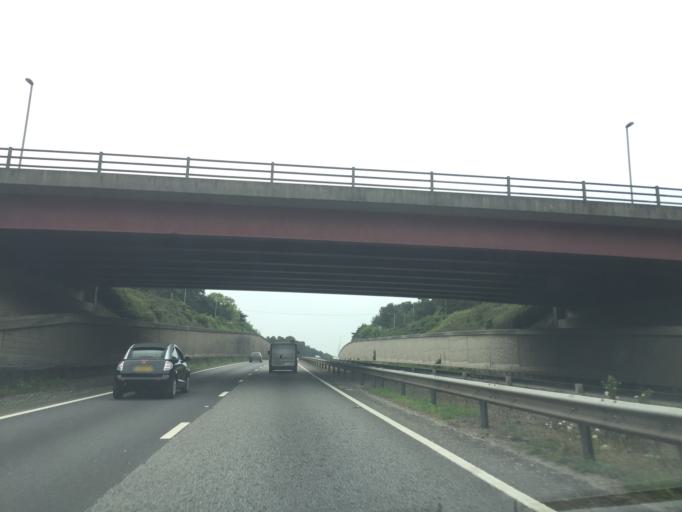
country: GB
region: England
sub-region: Hampshire
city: Ringwood
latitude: 50.8390
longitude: -1.8133
